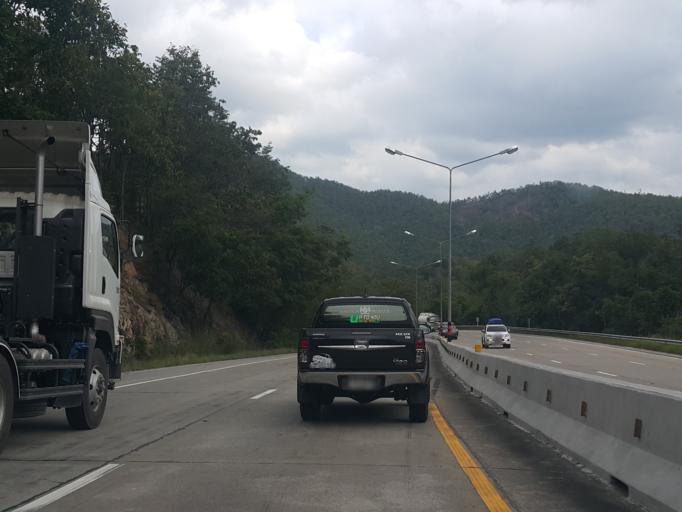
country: TH
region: Lamphun
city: Mae Tha
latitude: 18.4959
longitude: 99.1352
